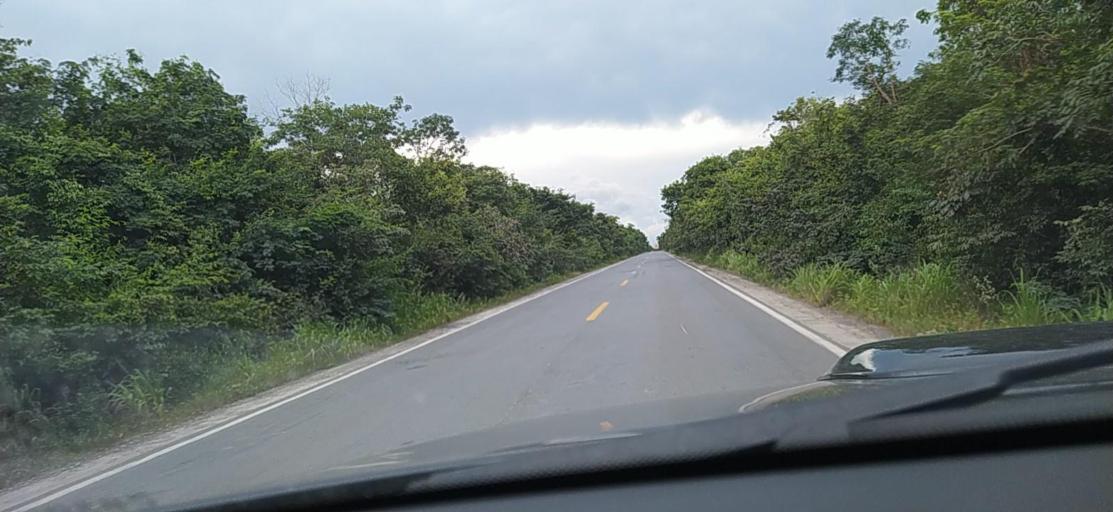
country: BR
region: Minas Gerais
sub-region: Francisco Sa
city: Francisco Sa
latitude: -16.2409
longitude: -43.6230
